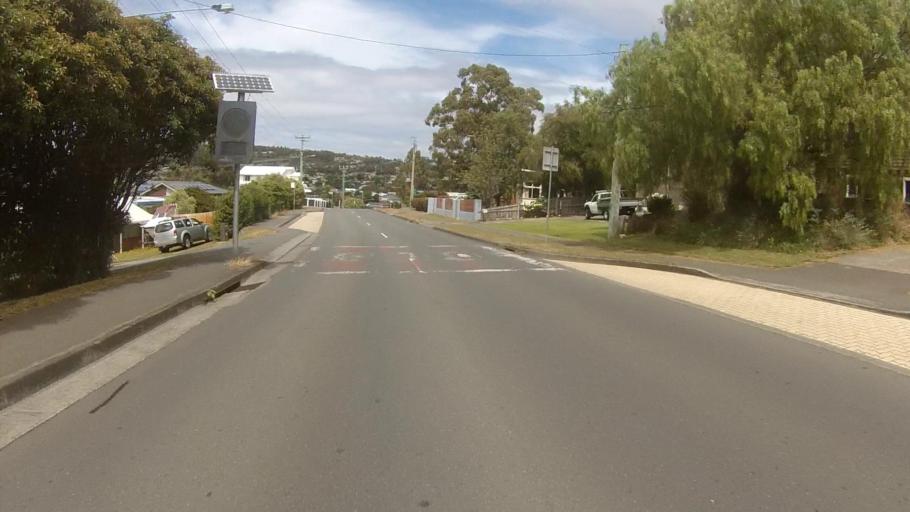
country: AU
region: Tasmania
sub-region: Kingborough
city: Blackmans Bay
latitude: -42.9960
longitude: 147.3233
